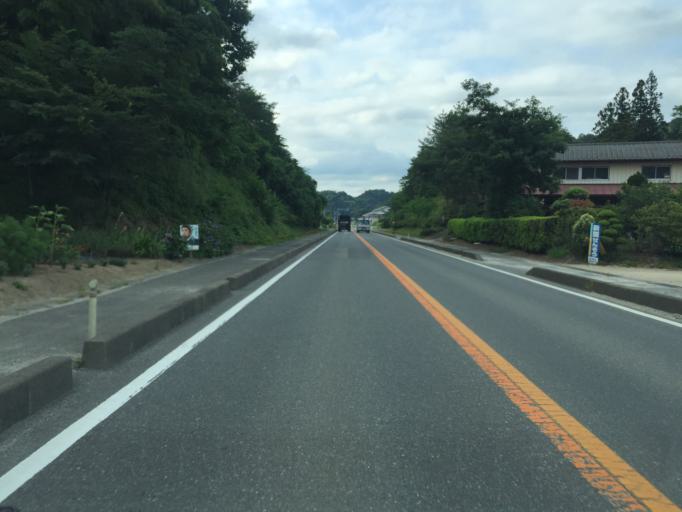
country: JP
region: Fukushima
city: Hobaramachi
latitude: 37.6938
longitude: 140.6088
